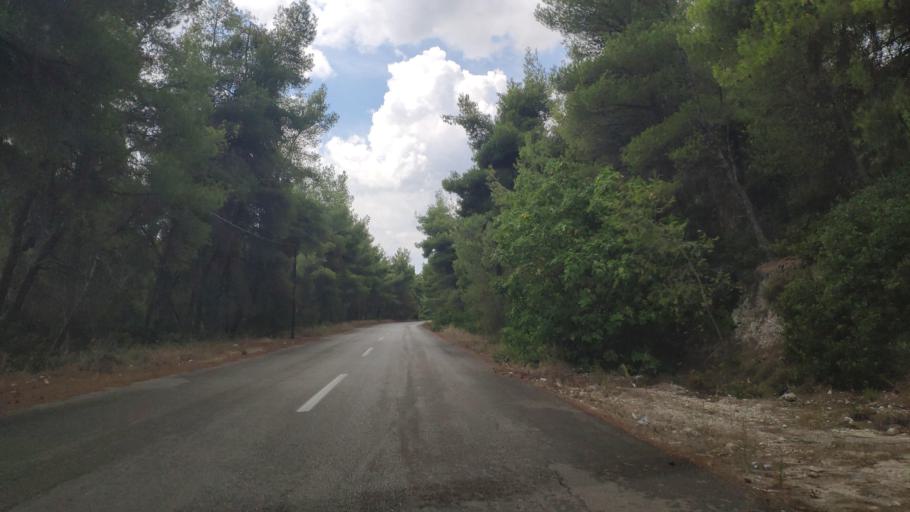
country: GR
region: Central Greece
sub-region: Nomos Fthiotidos
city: Malesina
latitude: 38.6415
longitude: 23.1977
